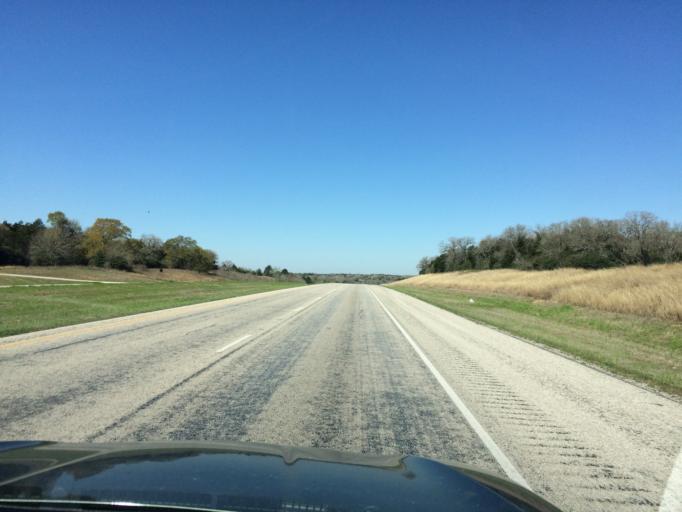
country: US
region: Texas
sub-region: Bastrop County
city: Smithville
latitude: 29.9448
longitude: -97.0707
